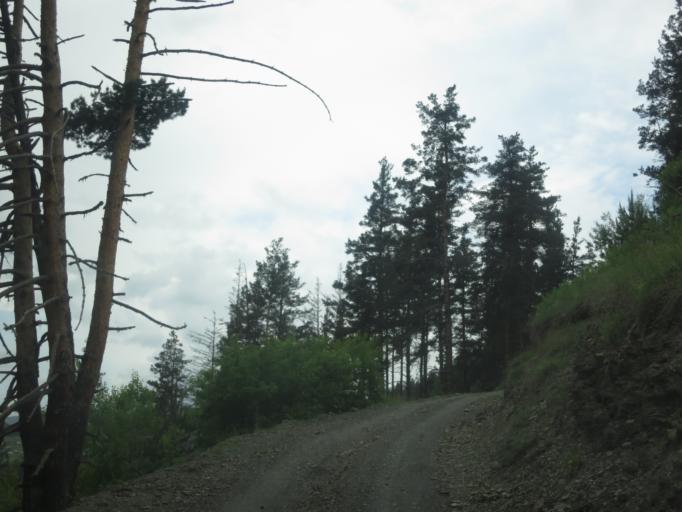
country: RU
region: Chechnya
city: Itum-Kali
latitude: 42.3618
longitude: 45.6551
